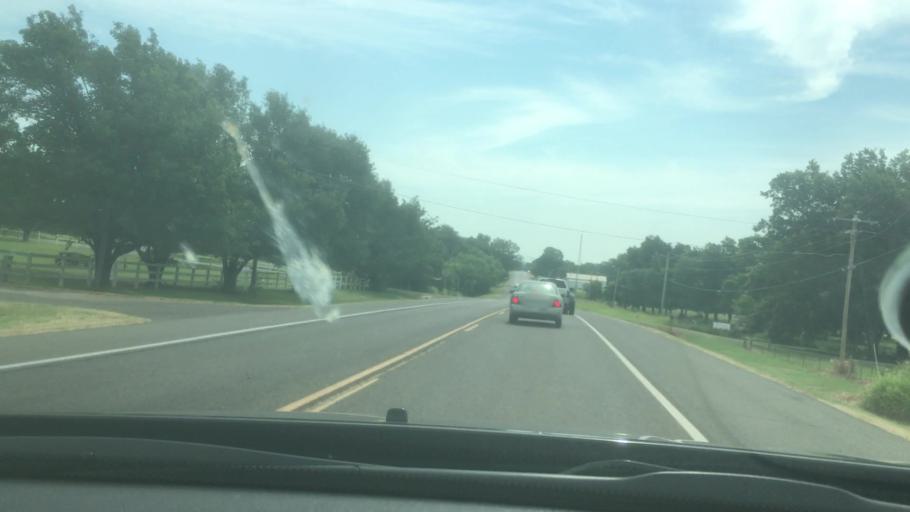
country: US
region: Oklahoma
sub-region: Garvin County
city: Maysville
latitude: 34.8173
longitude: -97.4272
